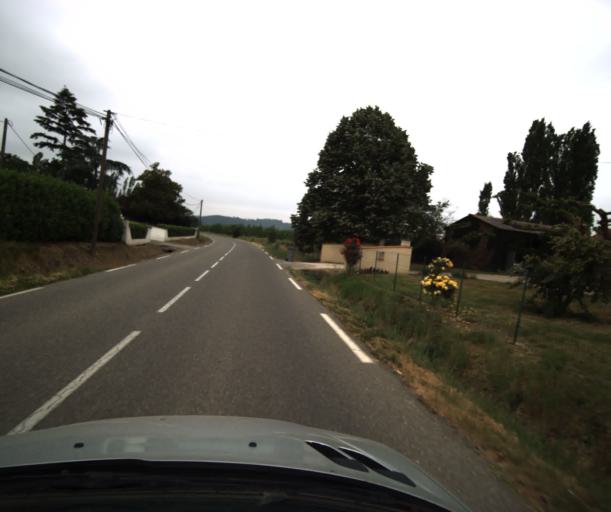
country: FR
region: Midi-Pyrenees
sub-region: Departement du Tarn-et-Garonne
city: Saint-Nicolas-de-la-Grave
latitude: 44.0722
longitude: 1.0038
